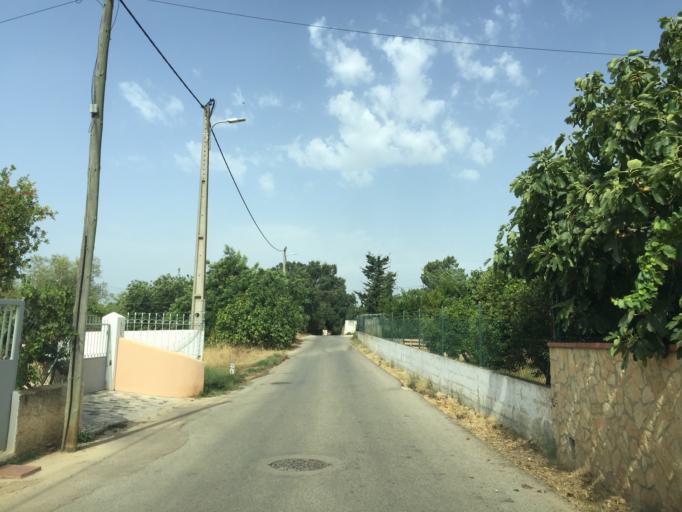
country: PT
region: Faro
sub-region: Loule
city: Vilamoura
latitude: 37.1029
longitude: -8.0989
